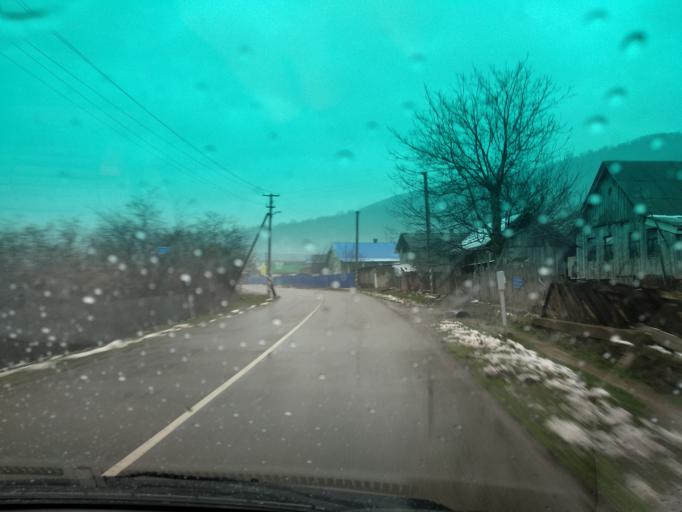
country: RU
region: Krasnodarskiy
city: Khadyzhensk
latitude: 44.2456
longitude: 39.3757
